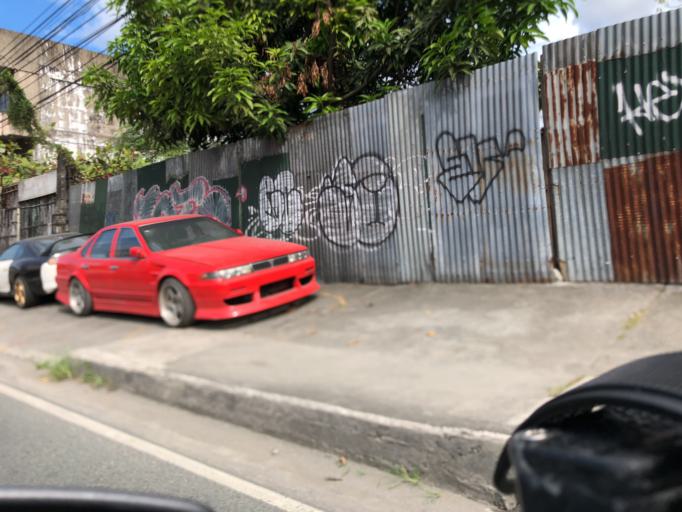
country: PH
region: Calabarzon
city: Bagong Pagasa
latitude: 14.7207
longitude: 121.0612
